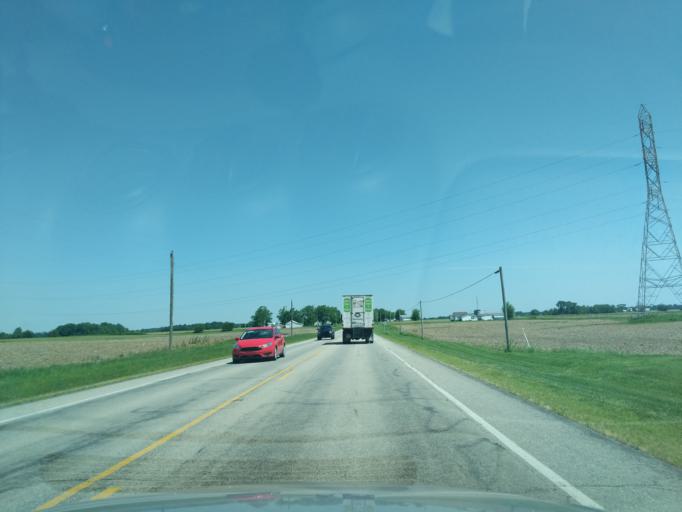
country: US
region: Indiana
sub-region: Whitley County
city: Columbia City
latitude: 41.0637
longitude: -85.4704
